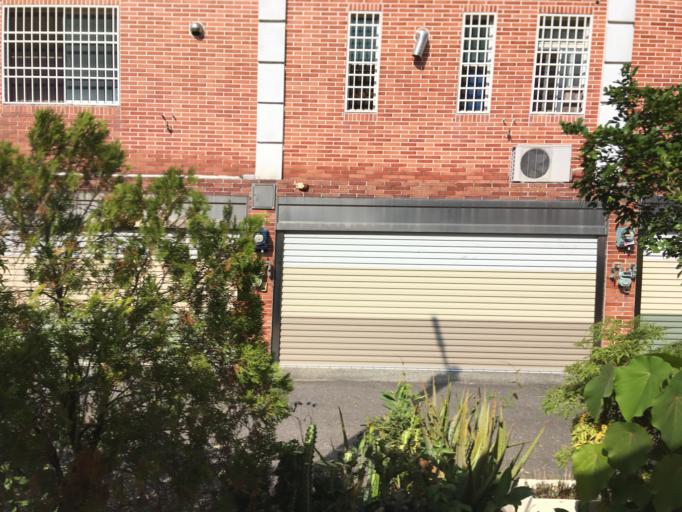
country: TW
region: Taiwan
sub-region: Chiayi
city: Jiayi Shi
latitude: 23.4899
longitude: 120.4621
